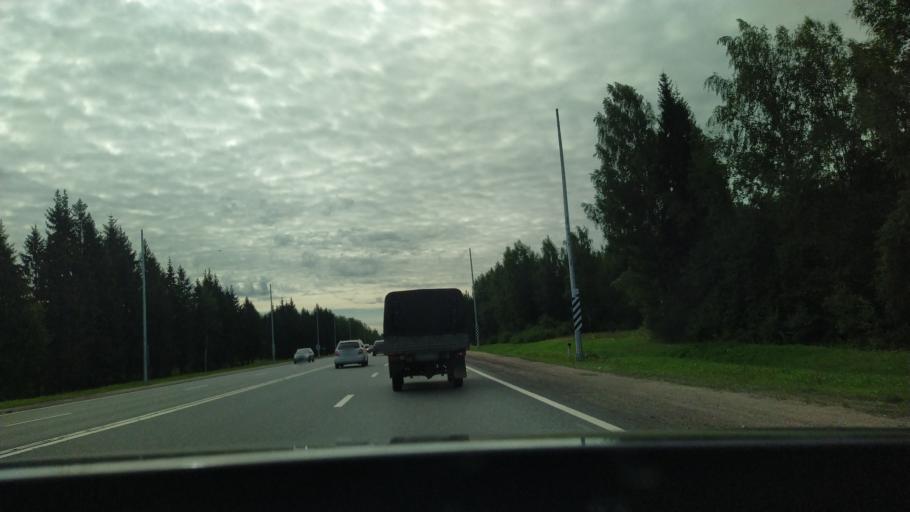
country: RU
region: Leningrad
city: Ul'yanovka
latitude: 59.5908
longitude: 30.7863
